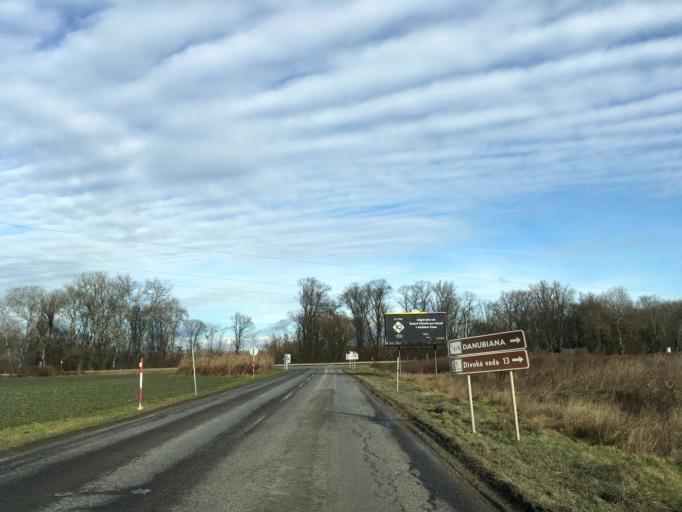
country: AT
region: Burgenland
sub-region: Politischer Bezirk Neusiedl am See
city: Kittsee
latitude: 48.0785
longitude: 17.1272
